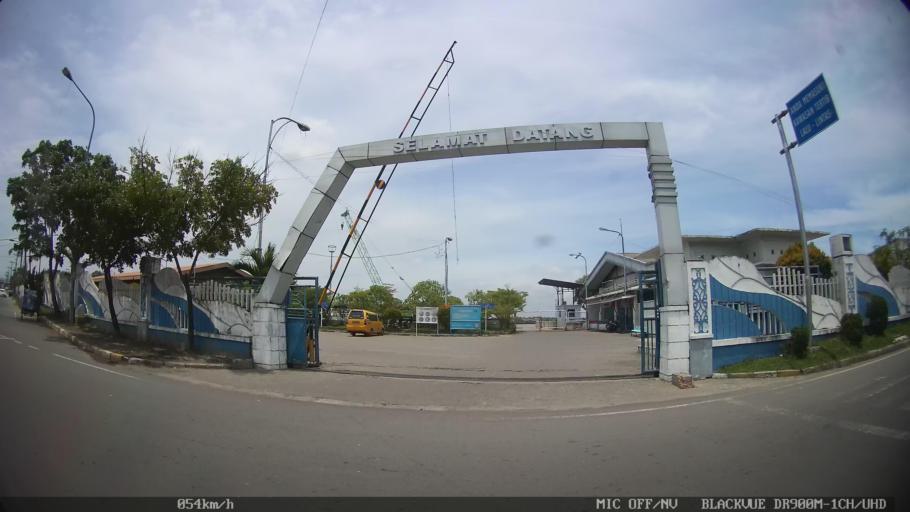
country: ID
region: North Sumatra
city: Belawan
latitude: 3.7788
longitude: 98.6813
